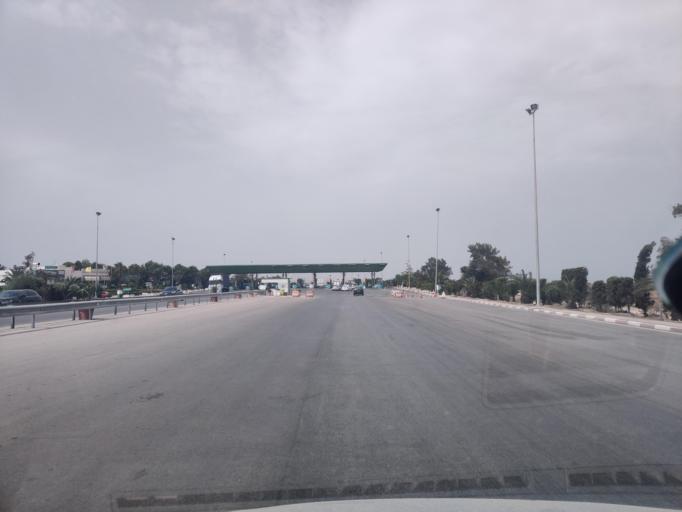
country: TN
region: Susah
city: Sidi Bou Ali
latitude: 36.0024
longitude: 10.4365
